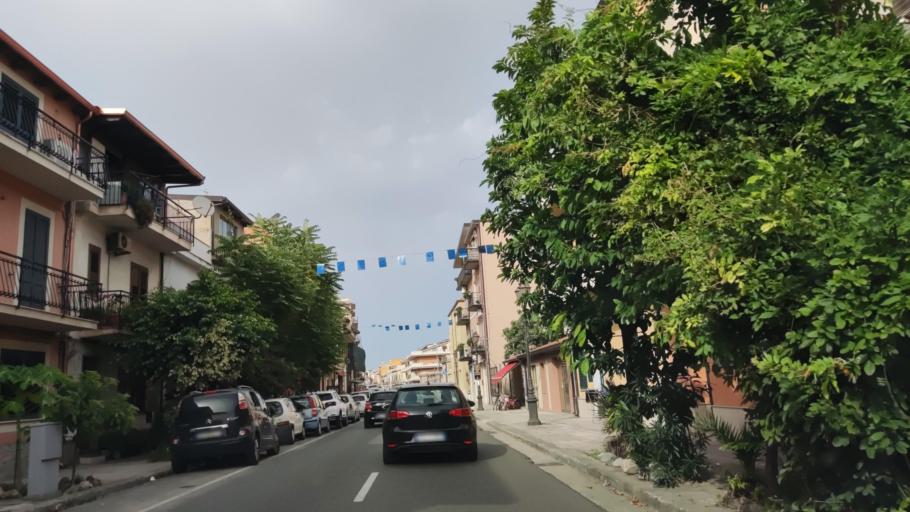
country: IT
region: Calabria
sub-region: Provincia di Reggio Calabria
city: Siderno
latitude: 38.2637
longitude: 16.2922
